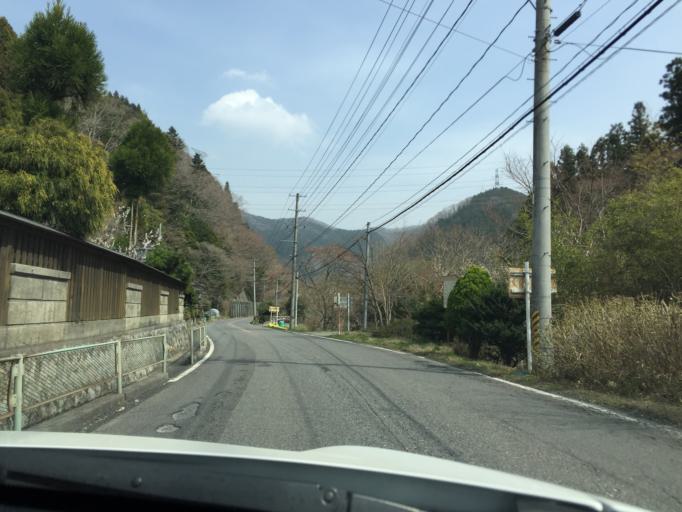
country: JP
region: Fukushima
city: Ishikawa
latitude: 37.0540
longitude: 140.6011
